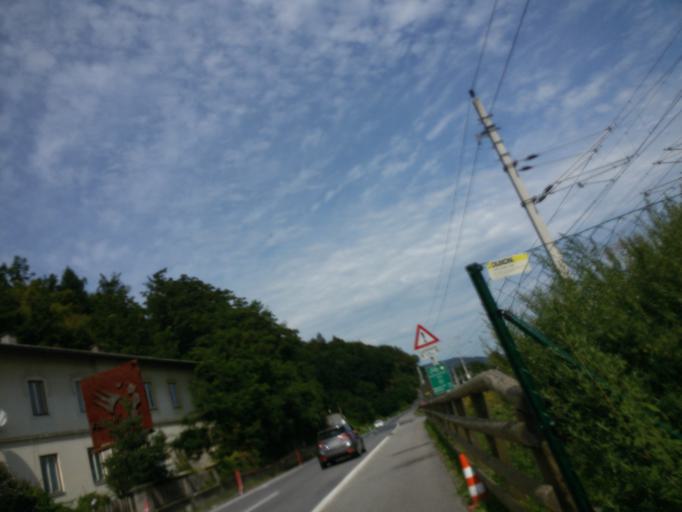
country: AT
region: Carinthia
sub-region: Politischer Bezirk Klagenfurt Land
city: Schiefling am See
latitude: 46.6274
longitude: 14.0908
